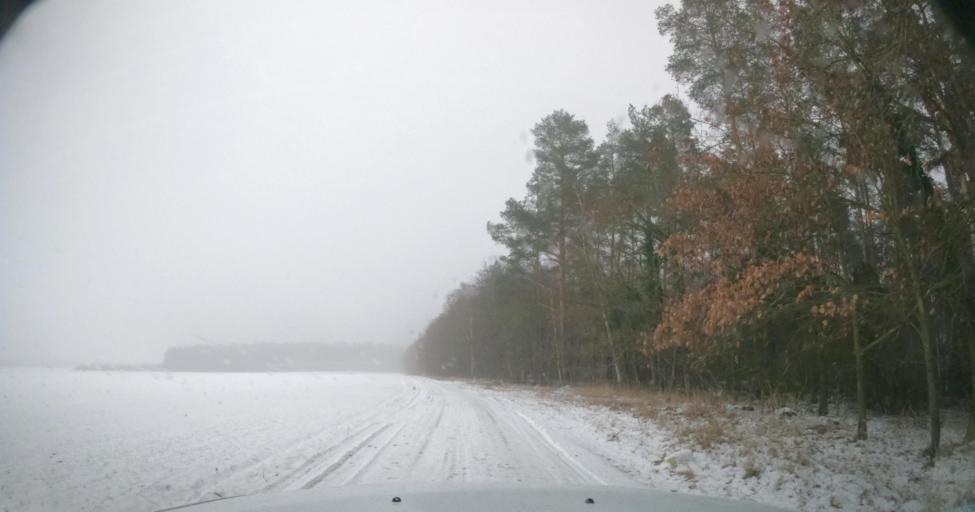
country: PL
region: West Pomeranian Voivodeship
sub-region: Powiat kamienski
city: Golczewo
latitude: 53.7681
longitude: 14.9196
